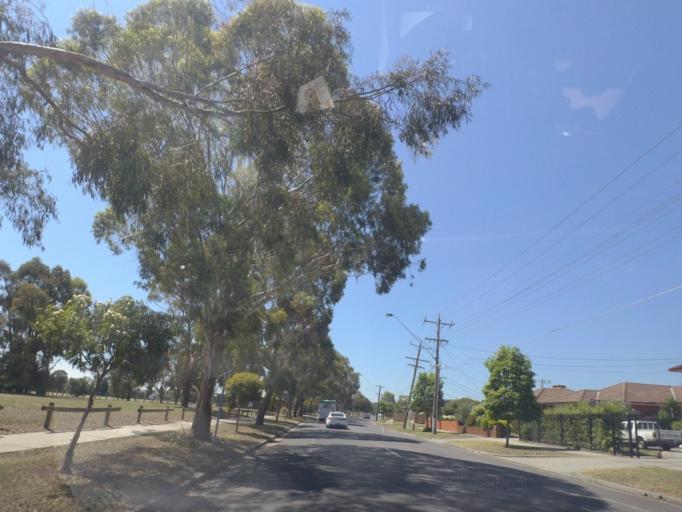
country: AU
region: Victoria
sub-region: Darebin
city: Reservoir
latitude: -37.6987
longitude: 144.9901
